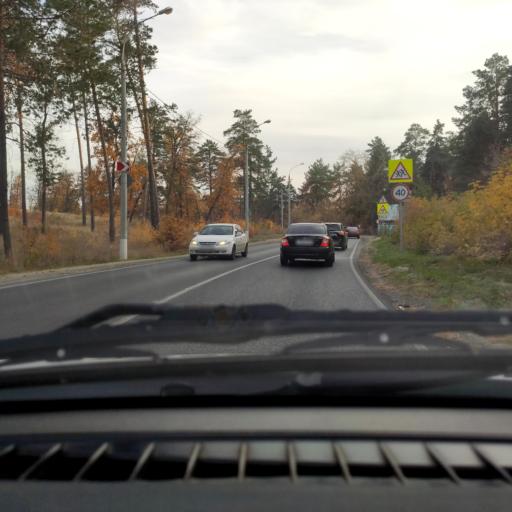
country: RU
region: Samara
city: Tol'yatti
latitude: 53.4877
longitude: 49.3110
